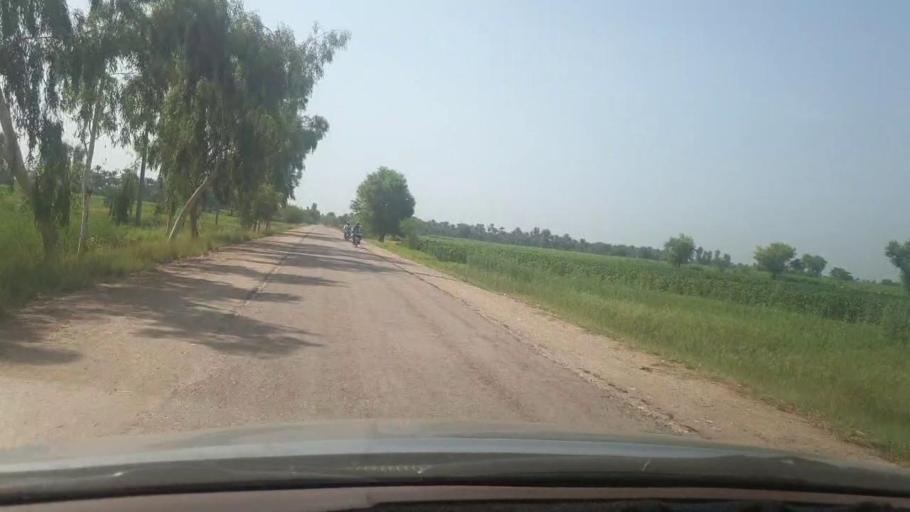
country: PK
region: Sindh
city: Ranipur
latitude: 27.2903
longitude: 68.5760
